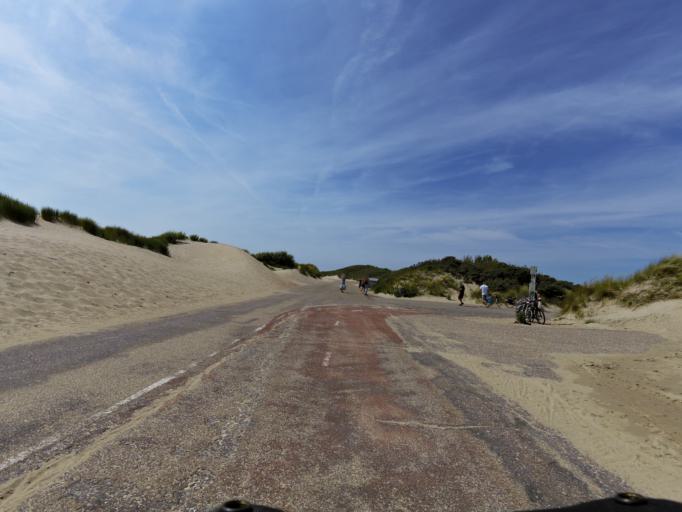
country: NL
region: Zeeland
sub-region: Schouwen-Duiveland
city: Burgh
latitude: 51.6672
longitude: 3.7144
